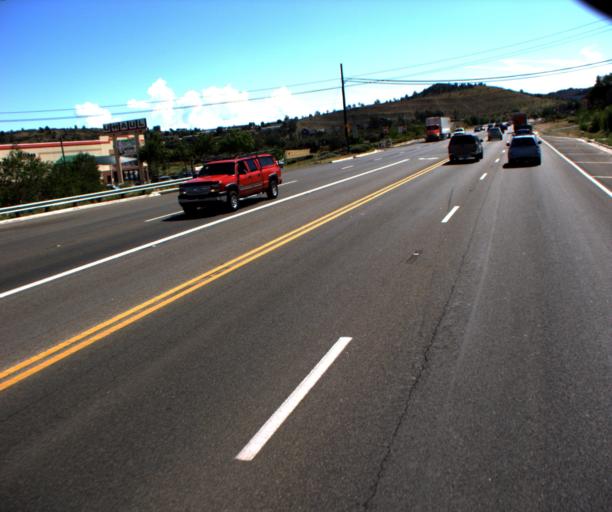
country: US
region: Arizona
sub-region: Yavapai County
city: Prescott
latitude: 34.5523
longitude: -112.4293
